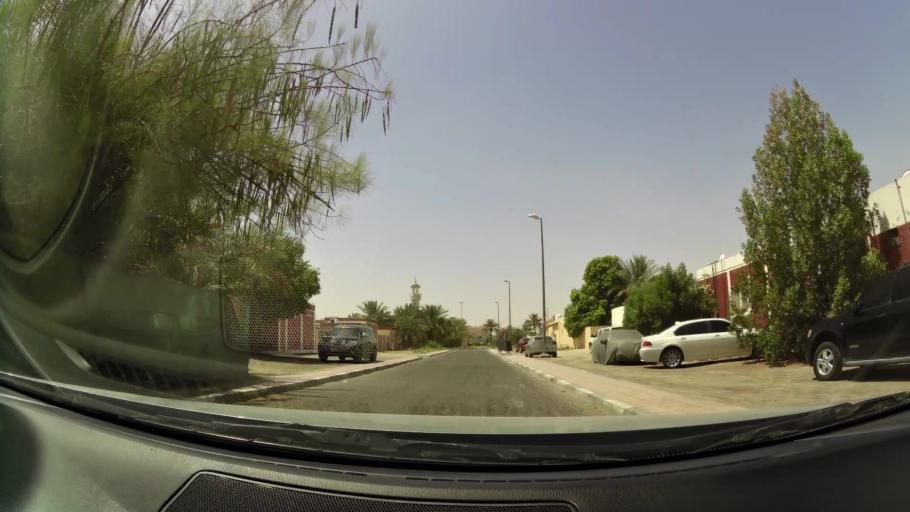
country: OM
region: Al Buraimi
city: Al Buraymi
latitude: 24.2760
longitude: 55.7747
